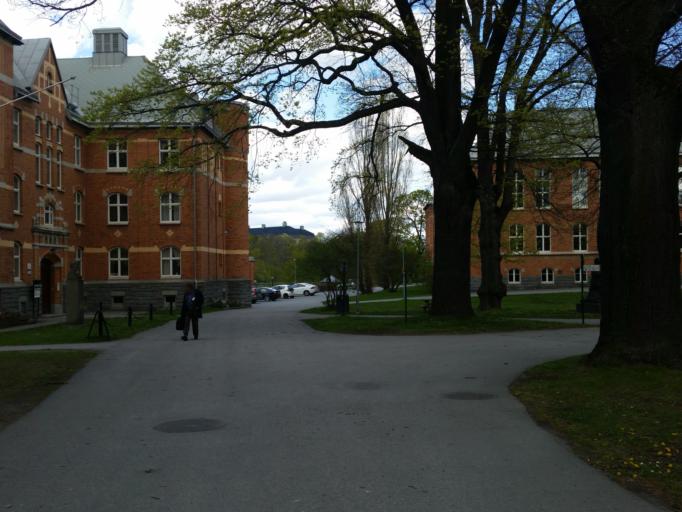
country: SE
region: Stockholm
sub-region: Stockholms Kommun
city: Stockholm
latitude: 59.3577
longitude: 18.0530
